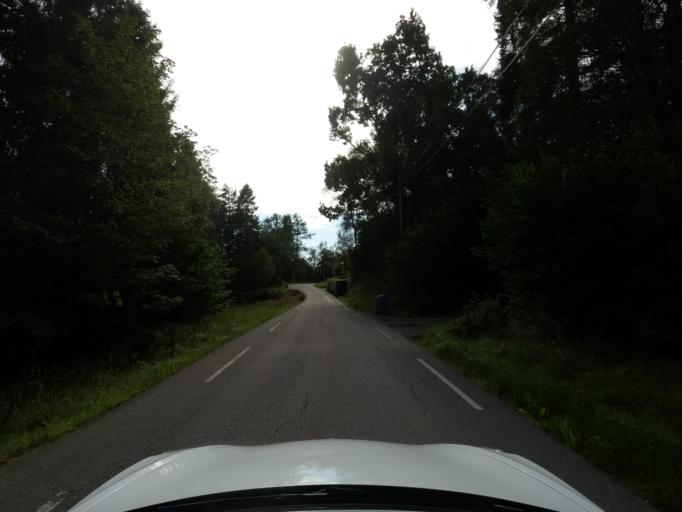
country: NO
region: Hordaland
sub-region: Bergen
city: Ytrebygda
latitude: 60.2749
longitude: 5.2422
